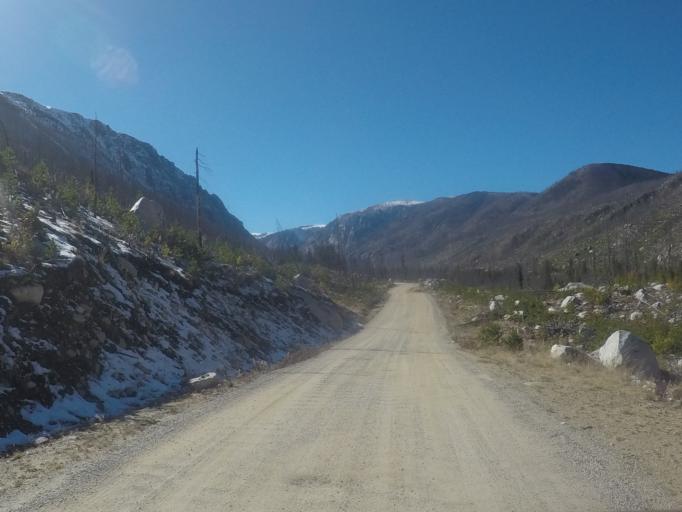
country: US
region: Montana
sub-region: Carbon County
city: Red Lodge
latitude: 45.1717
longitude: -109.4609
